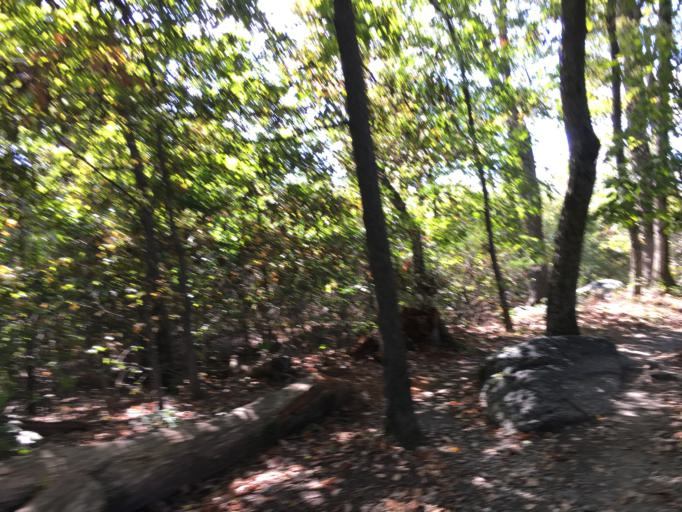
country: US
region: Pennsylvania
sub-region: York County
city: Yorklyn
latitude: 40.0099
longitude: -76.6452
